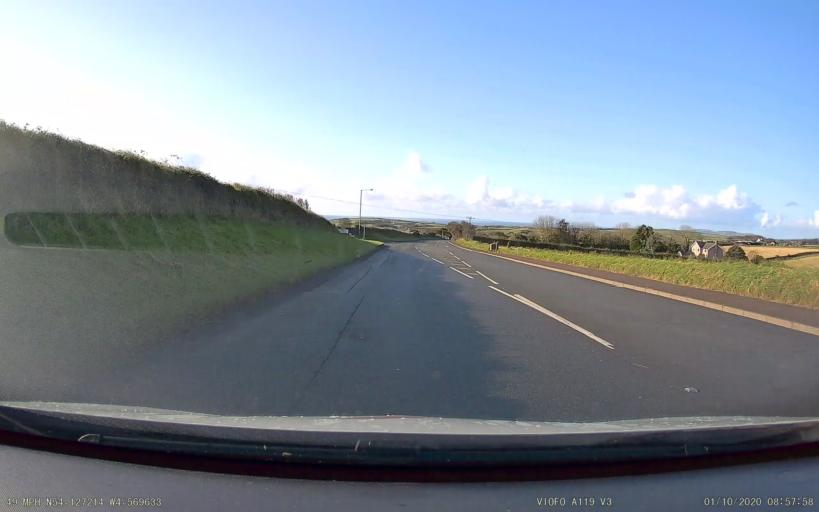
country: IM
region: Douglas
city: Douglas
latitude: 54.1272
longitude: -4.5696
